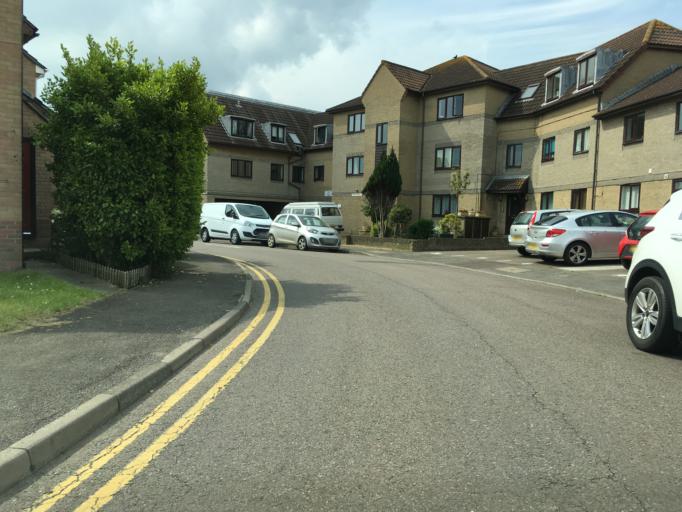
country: GB
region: England
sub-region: South Gloucestershire
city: Severn Beach
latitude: 51.5605
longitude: -2.6662
